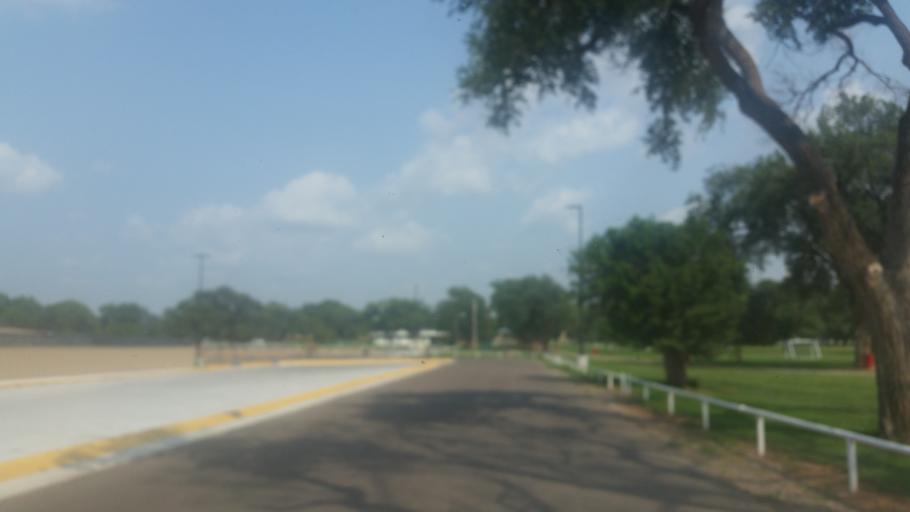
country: US
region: New Mexico
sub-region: Curry County
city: Clovis
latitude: 34.4079
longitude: -103.1843
